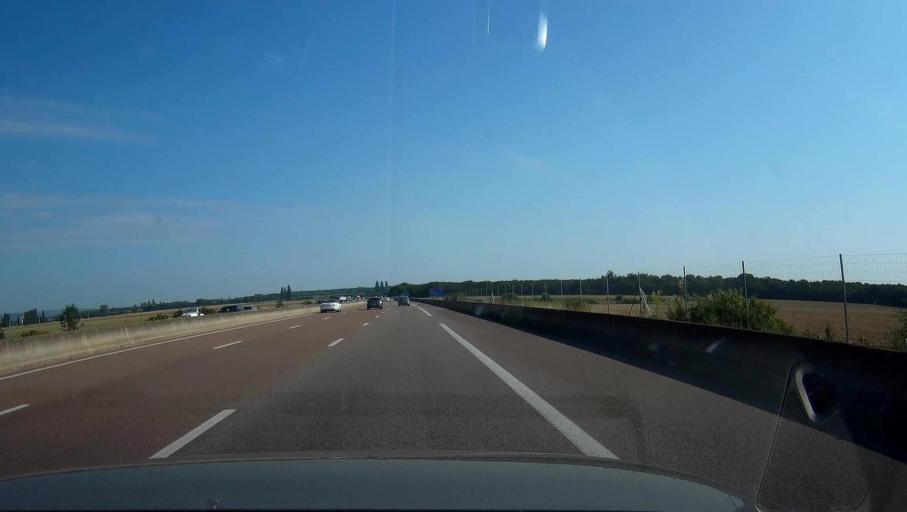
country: FR
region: Bourgogne
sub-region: Departement de la Cote-d'Or
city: Nuits-Saint-Georges
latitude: 47.1555
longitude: 4.9963
